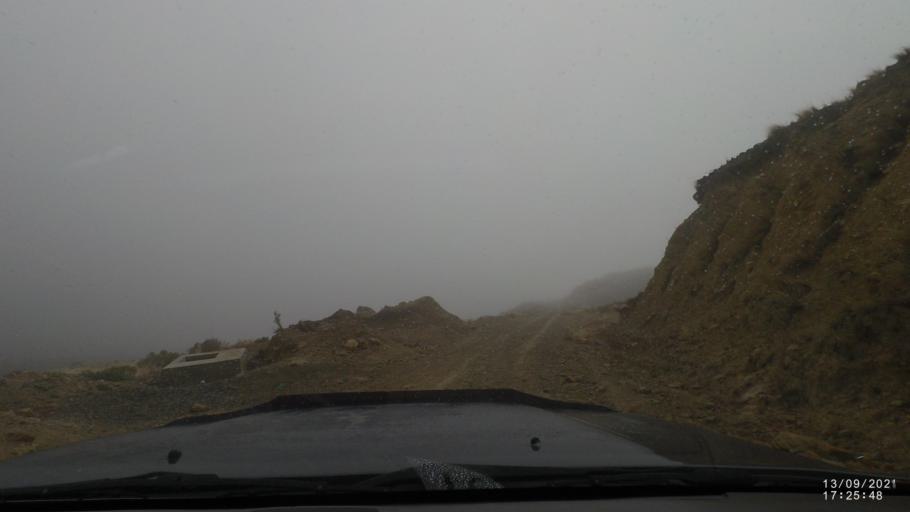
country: BO
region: Cochabamba
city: Colomi
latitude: -17.3604
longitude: -65.7818
